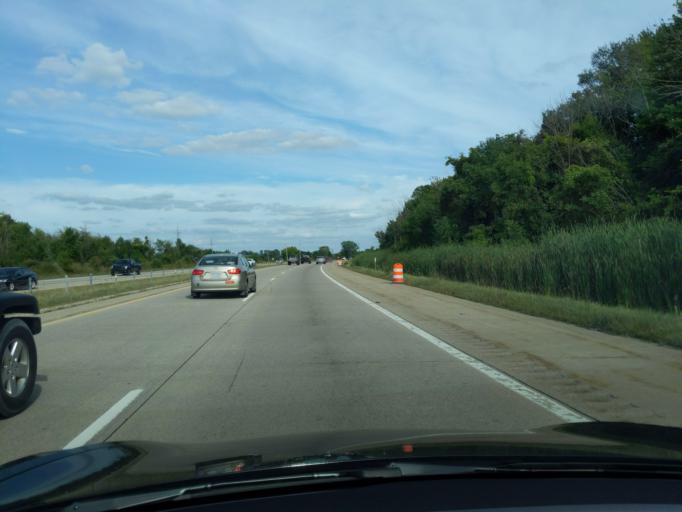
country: US
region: Michigan
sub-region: Ottawa County
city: Coopersville
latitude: 43.0532
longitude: -85.8912
